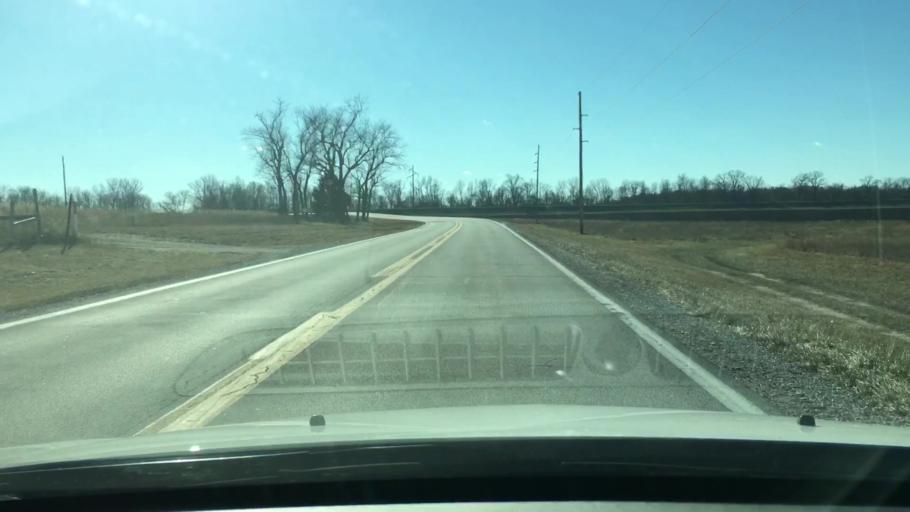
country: US
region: Illinois
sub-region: Cass County
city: Beardstown
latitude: 39.9362
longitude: -90.4930
